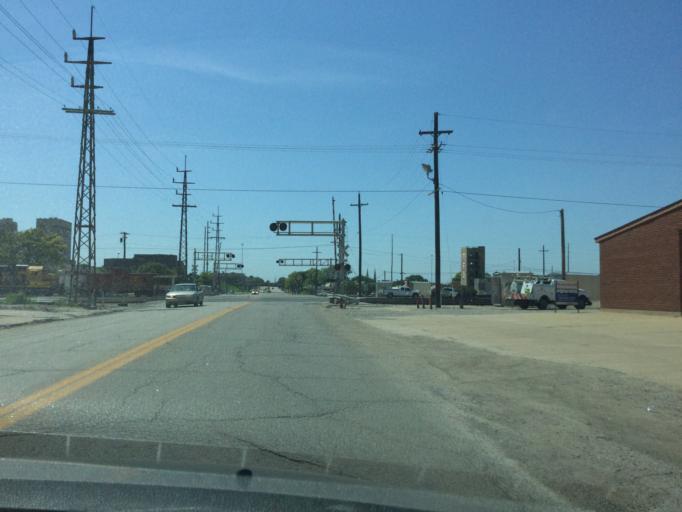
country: US
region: Kansas
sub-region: Shawnee County
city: Topeka
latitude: 39.0521
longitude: -95.6628
